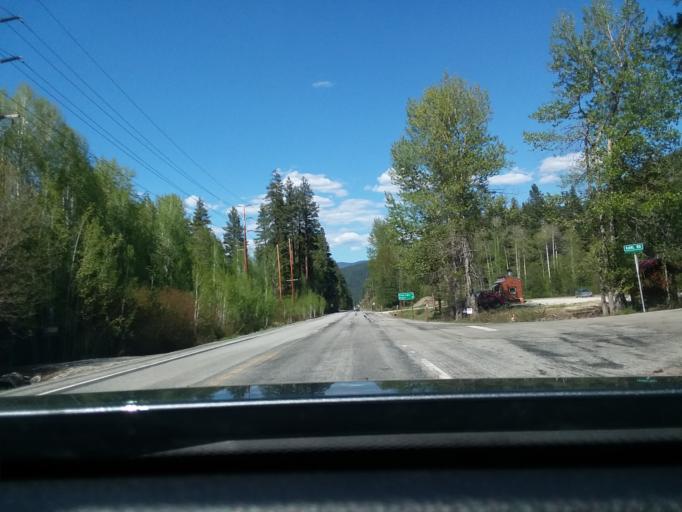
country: US
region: Washington
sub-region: Chelan County
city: Leavenworth
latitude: 47.7580
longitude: -120.7375
